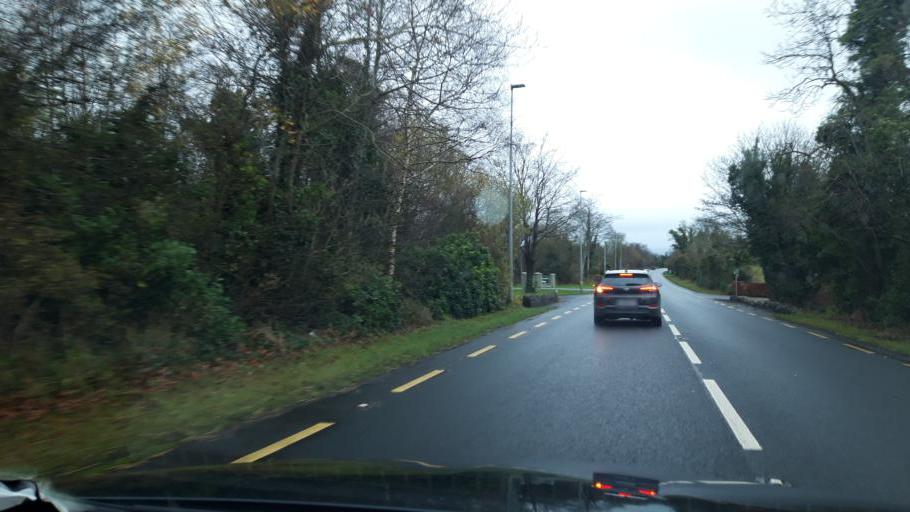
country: IE
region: Ulster
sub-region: County Monaghan
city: Castleblayney
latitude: 54.1077
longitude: -6.7176
